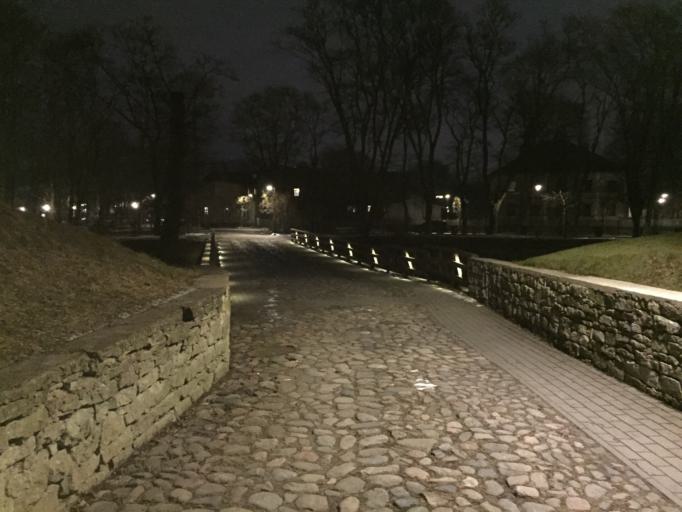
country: EE
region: Saare
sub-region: Kuressaare linn
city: Kuressaare
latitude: 58.2485
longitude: 22.4812
